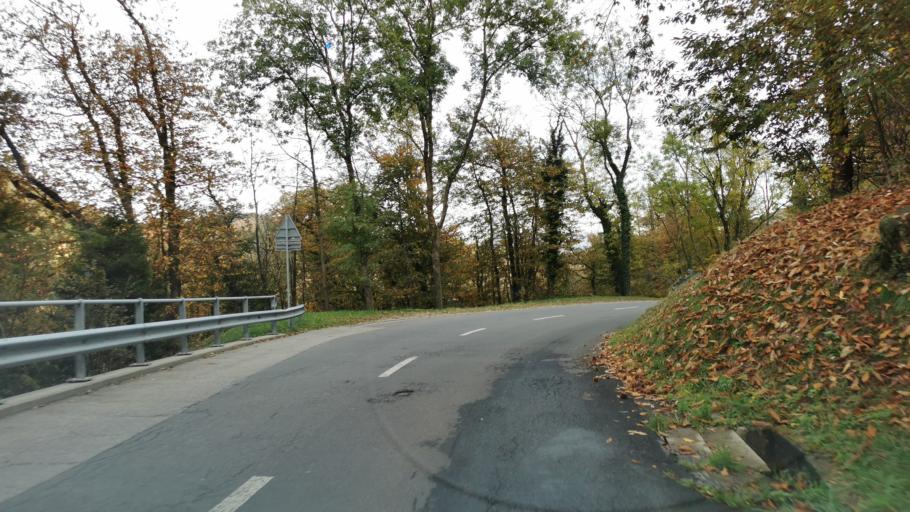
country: CH
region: Ticino
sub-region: Lugano District
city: Pura
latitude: 46.0170
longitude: 8.8547
